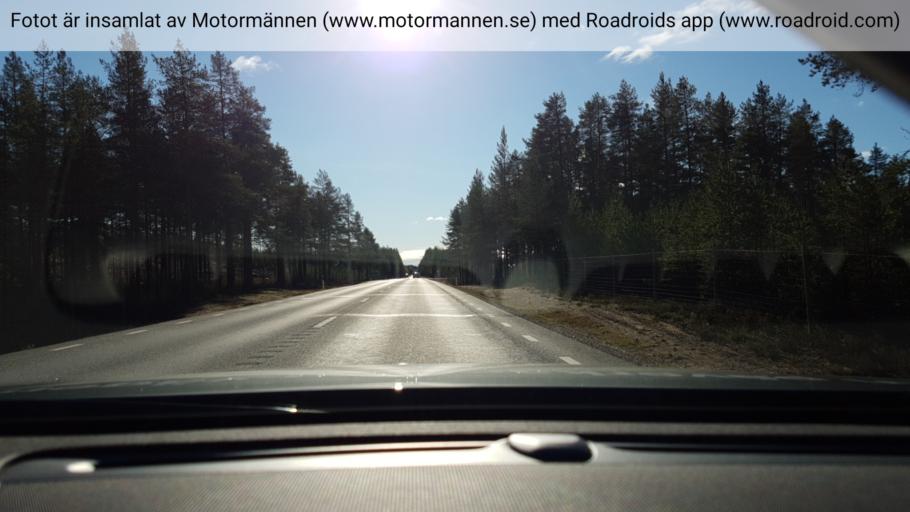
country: SE
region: Vaesterbotten
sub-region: Skelleftea Kommun
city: Burea
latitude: 64.5651
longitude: 21.2304
